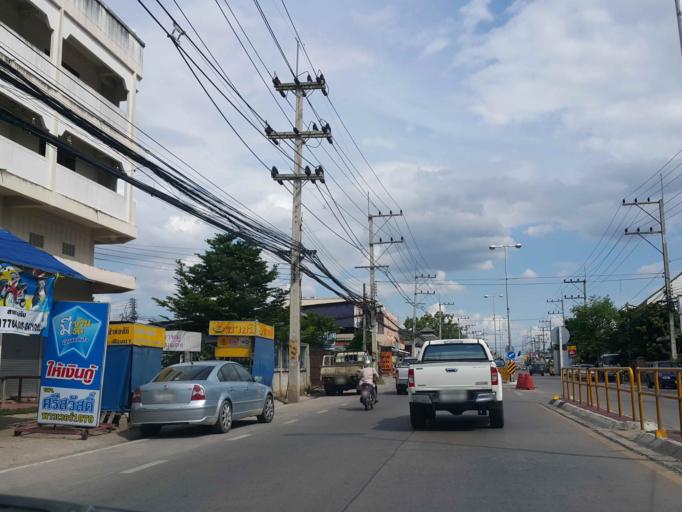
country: TH
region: Chiang Mai
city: San Sai
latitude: 18.9137
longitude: 98.9456
